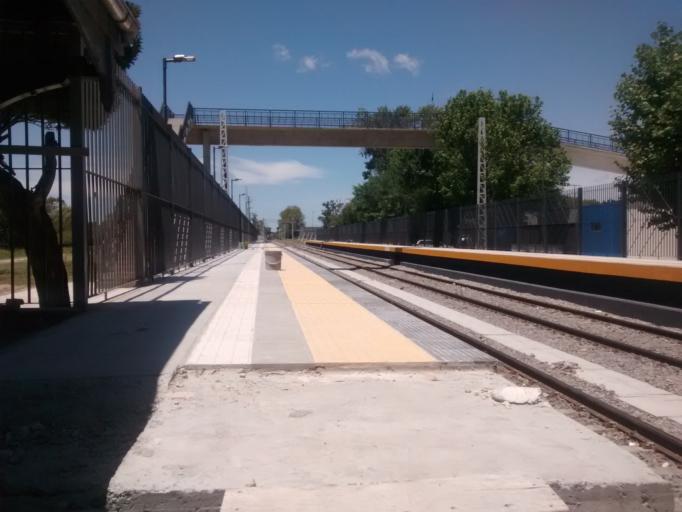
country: AR
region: Buenos Aires
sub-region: Partido de La Plata
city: La Plata
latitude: -34.8657
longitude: -58.0421
